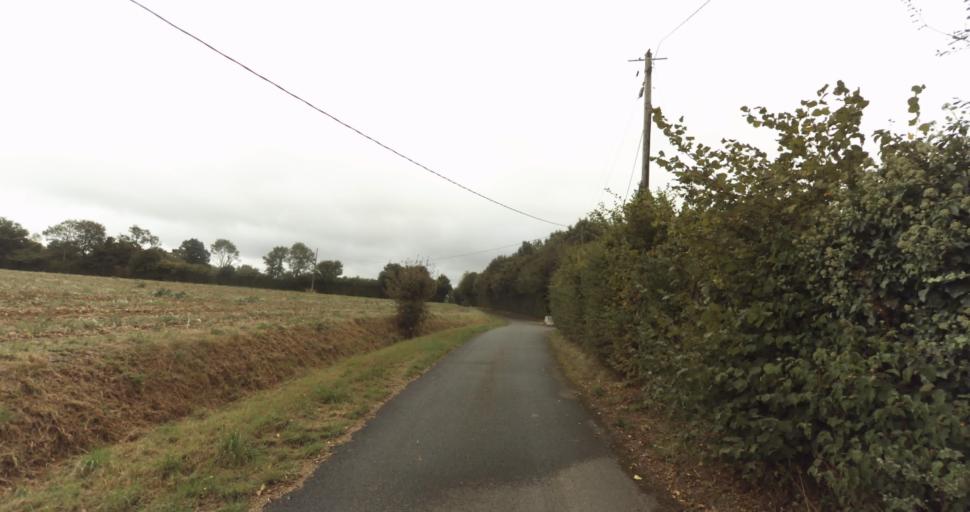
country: FR
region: Lower Normandy
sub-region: Departement de l'Orne
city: Sainte-Gauburge-Sainte-Colombe
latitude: 48.7189
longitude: 0.4452
